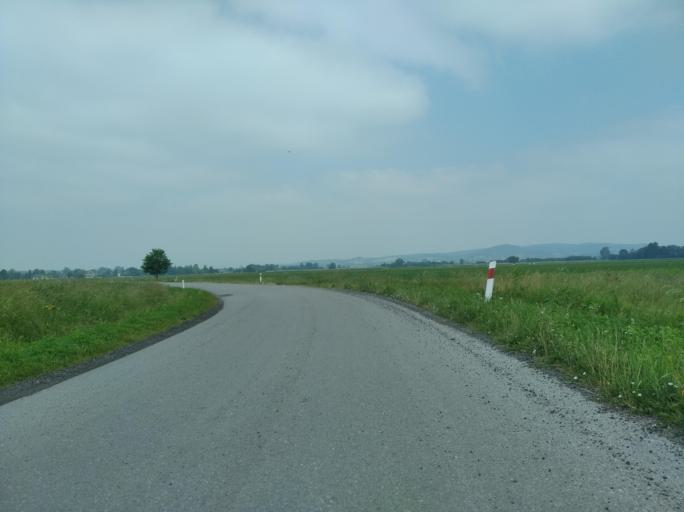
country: PL
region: Subcarpathian Voivodeship
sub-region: Powiat sanocki
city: Besko
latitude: 49.6109
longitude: 21.9555
